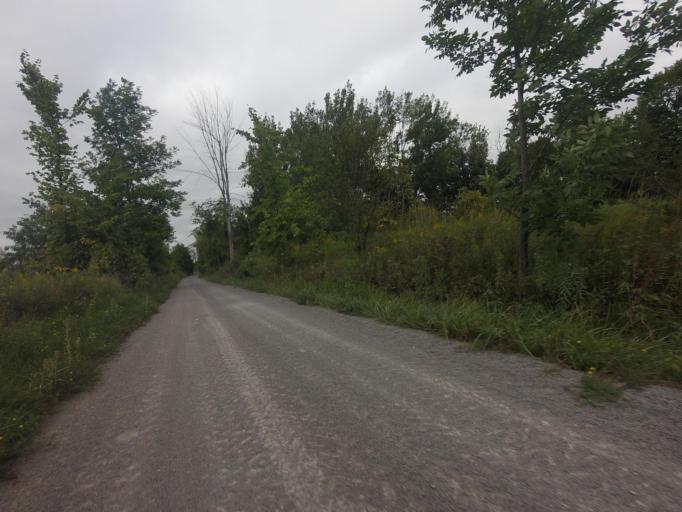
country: CA
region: Ontario
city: Omemee
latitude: 44.4442
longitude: -78.7693
